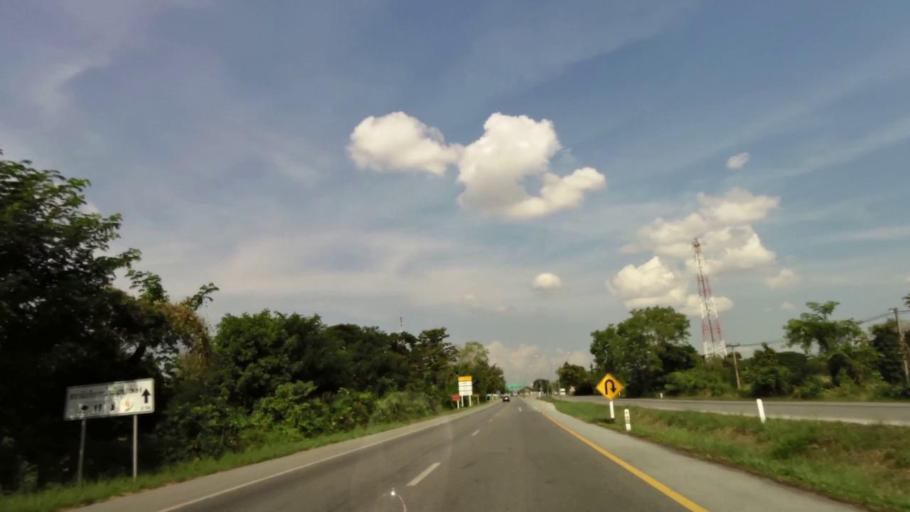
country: TH
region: Uttaradit
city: Thong Saen Khan
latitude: 17.4659
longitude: 100.2369
